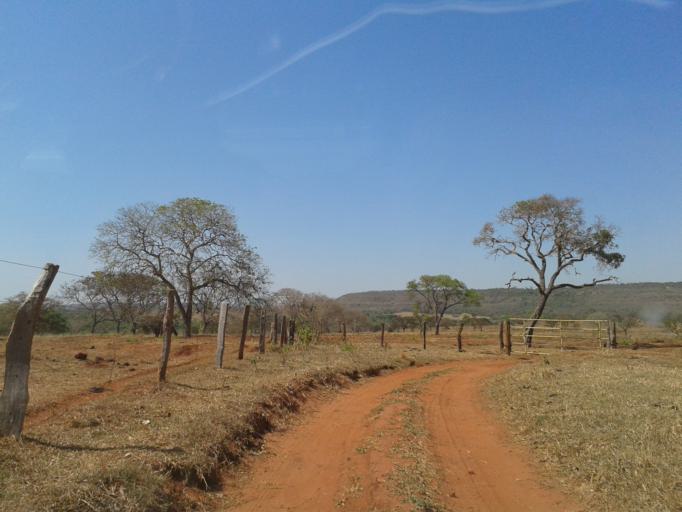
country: BR
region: Minas Gerais
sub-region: Ituiutaba
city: Ituiutaba
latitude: -19.0570
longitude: -49.3751
